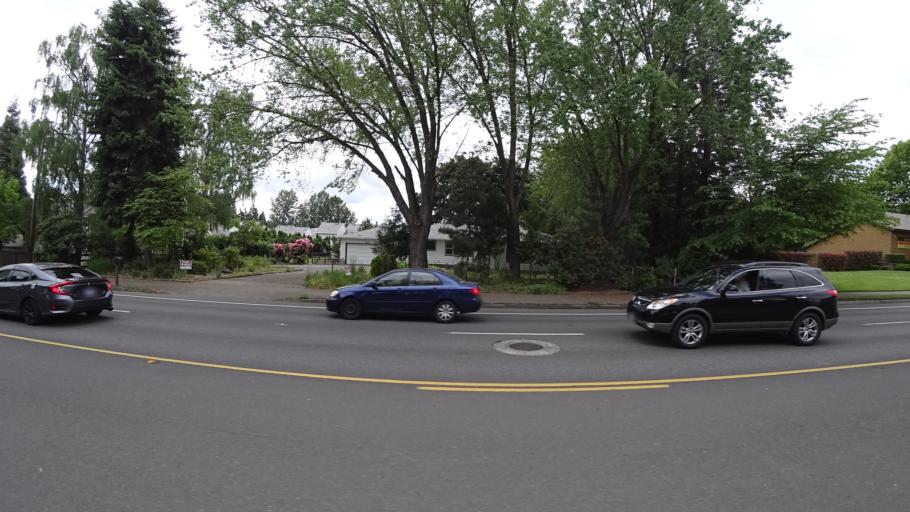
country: US
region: Oregon
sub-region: Washington County
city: Beaverton
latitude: 45.4827
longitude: -122.8261
